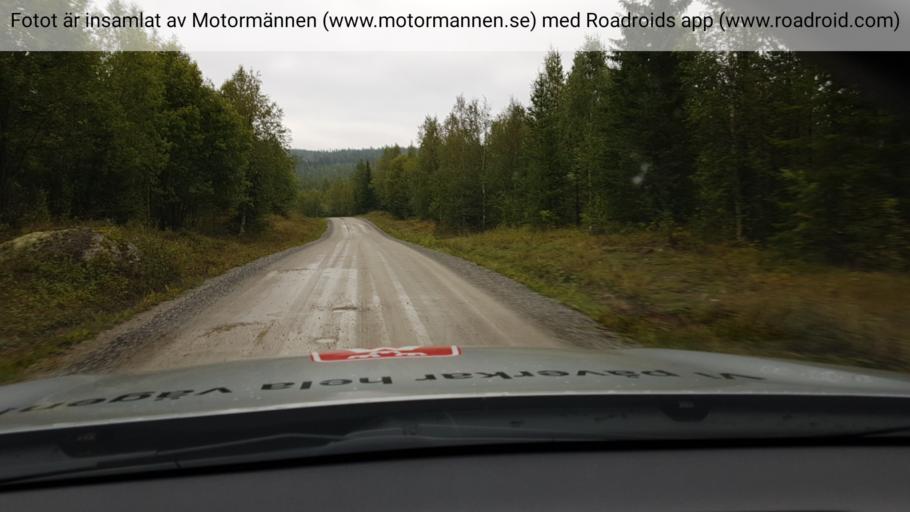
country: SE
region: Jaemtland
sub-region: Braecke Kommun
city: Braecke
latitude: 62.7418
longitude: 15.4971
